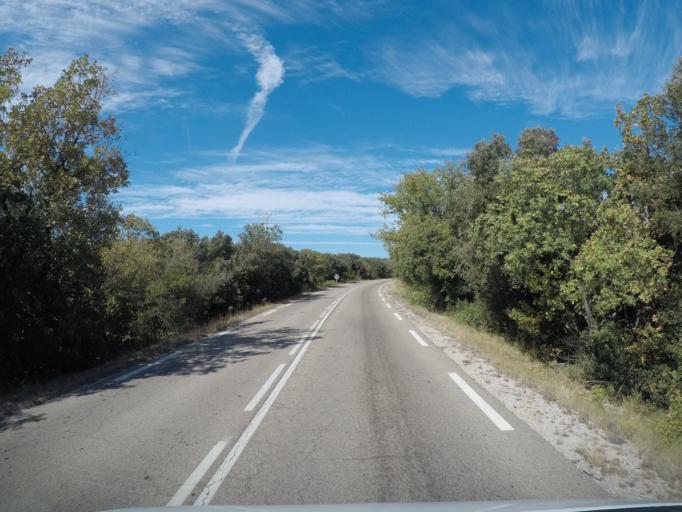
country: FR
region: Languedoc-Roussillon
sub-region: Departement de l'Herault
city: Saint-Martin-de-Londres
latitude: 43.7650
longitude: 3.7460
